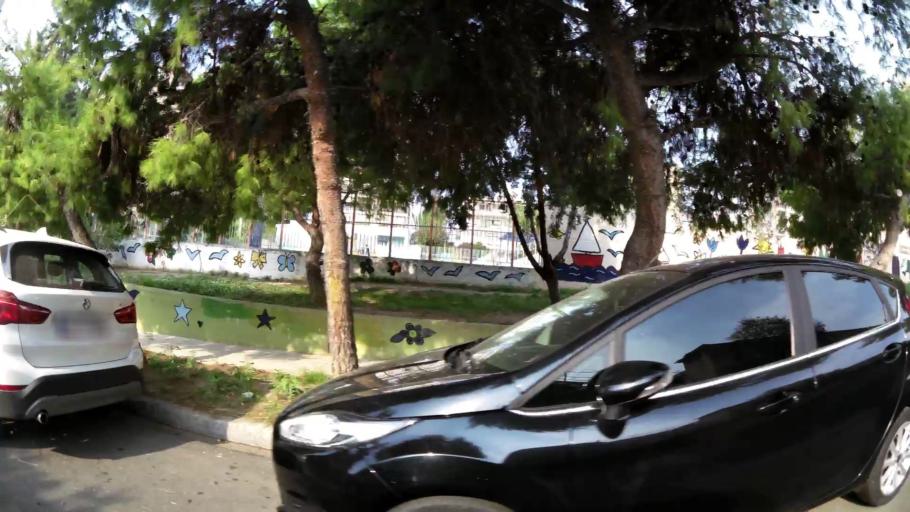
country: GR
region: Attica
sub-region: Nomarchia Athinas
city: Agios Dimitrios
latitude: 37.9278
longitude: 23.7191
